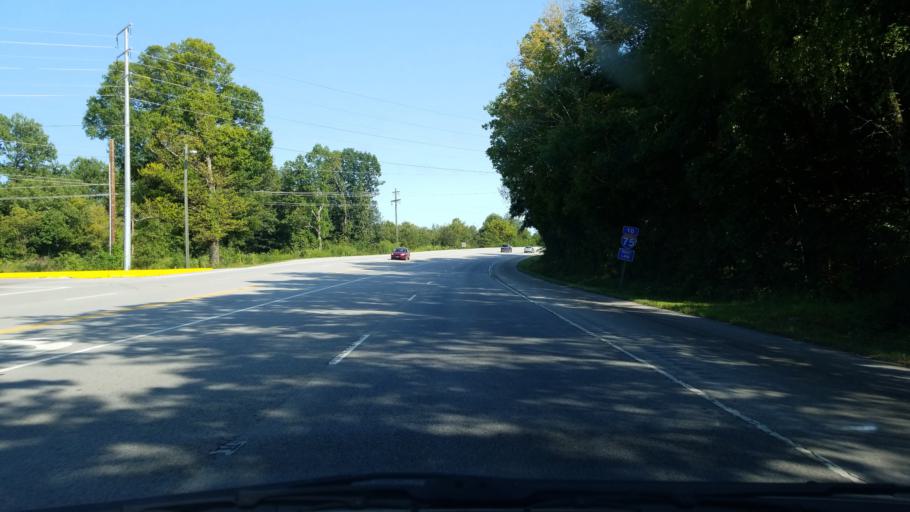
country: US
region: Tennessee
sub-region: Hamilton County
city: East Chattanooga
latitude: 35.0928
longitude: -85.2276
